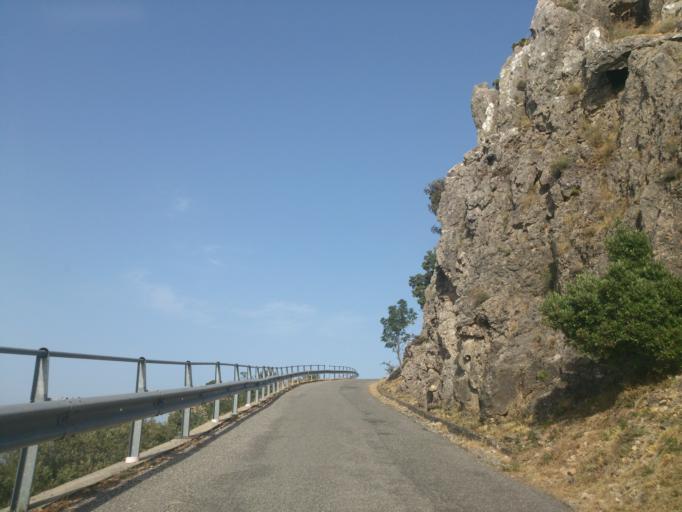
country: IT
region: Calabria
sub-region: Provincia di Reggio Calabria
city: Pazzano
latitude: 38.4659
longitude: 16.4392
